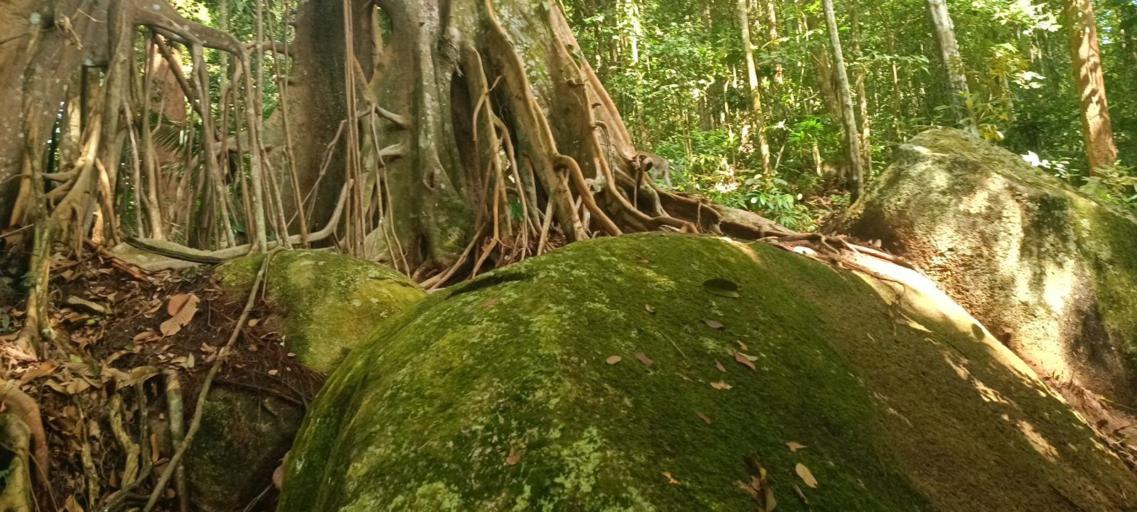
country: MY
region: Penang
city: Bukit Mertajam
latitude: 5.3673
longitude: 100.4856
